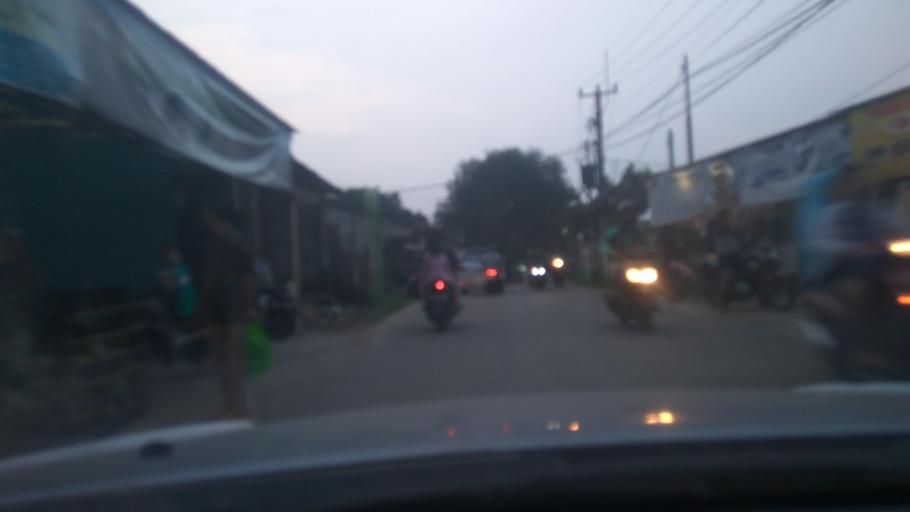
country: ID
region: West Java
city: Pamulang
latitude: -6.3679
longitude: 106.7344
